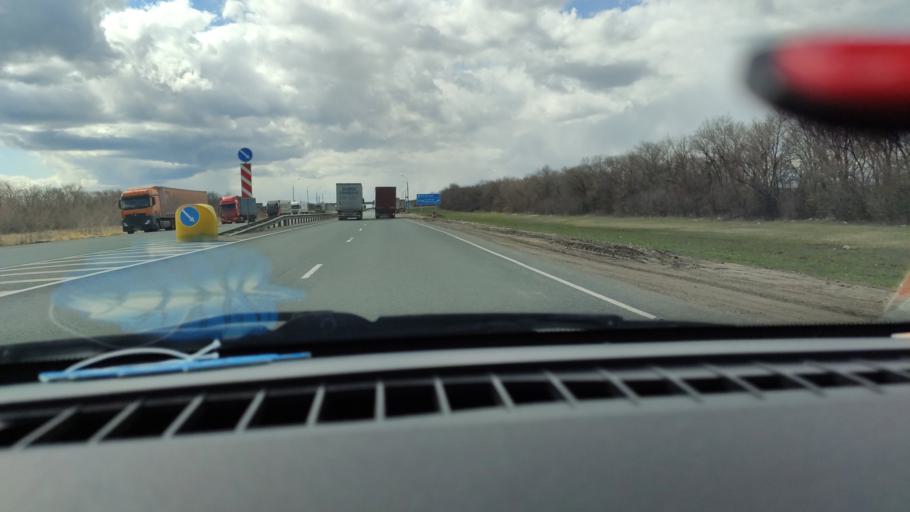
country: RU
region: Samara
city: Varlamovo
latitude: 53.1965
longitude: 48.2966
